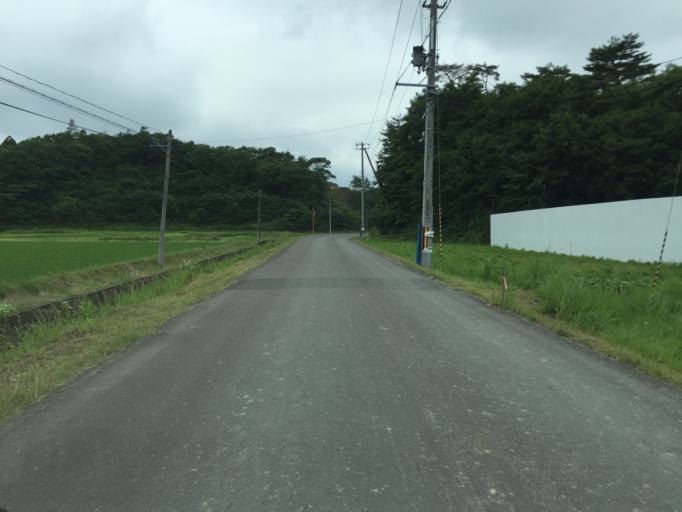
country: JP
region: Fukushima
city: Namie
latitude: 37.7281
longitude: 140.9562
